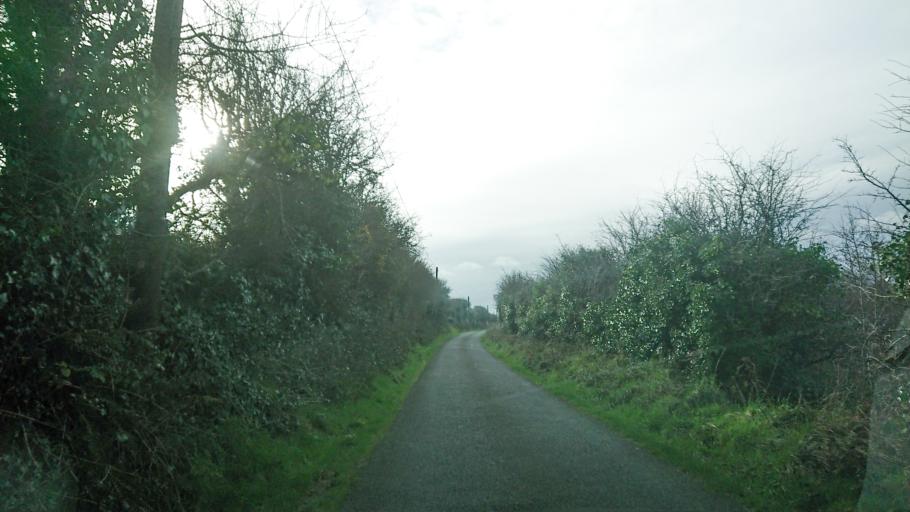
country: IE
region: Munster
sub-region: Waterford
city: Tra Mhor
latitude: 52.1539
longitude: -7.1912
